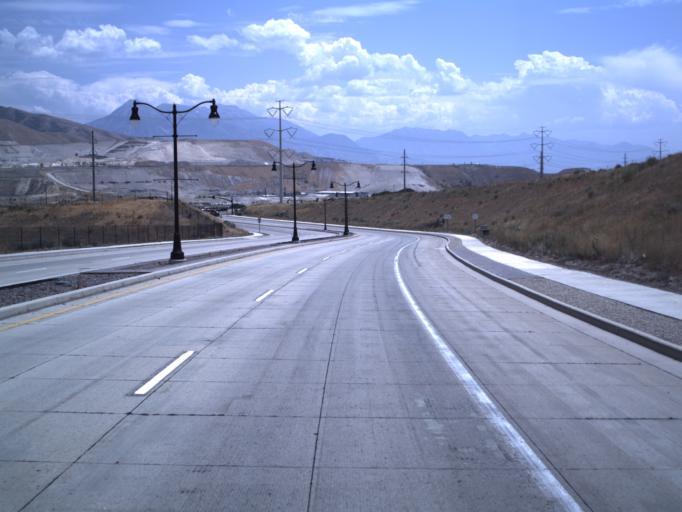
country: US
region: Utah
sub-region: Salt Lake County
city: Bluffdale
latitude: 40.4634
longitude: -111.9467
